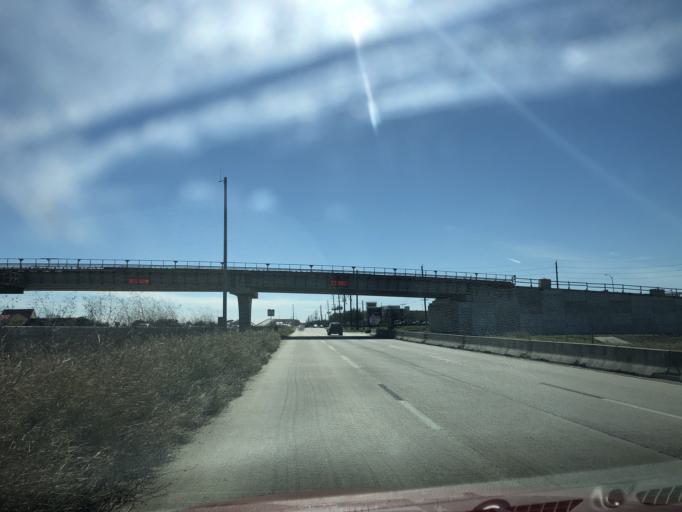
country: US
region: Texas
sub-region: Brazoria County
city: Brookside Village
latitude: 29.5713
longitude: -95.3870
